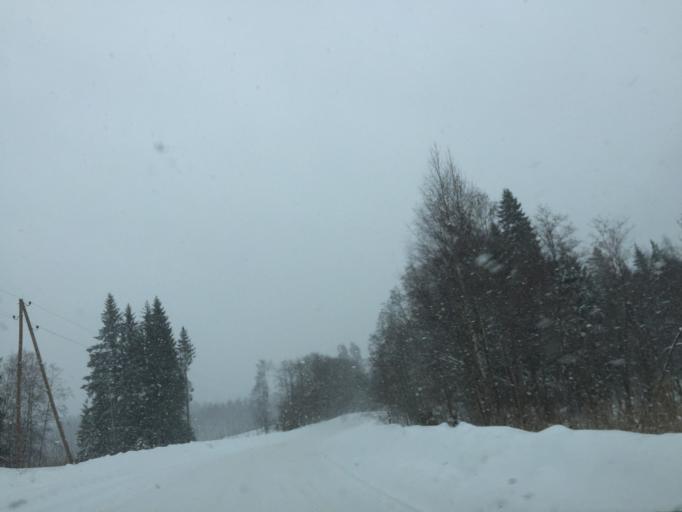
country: LV
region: Amatas Novads
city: Drabesi
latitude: 57.0720
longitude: 25.3357
